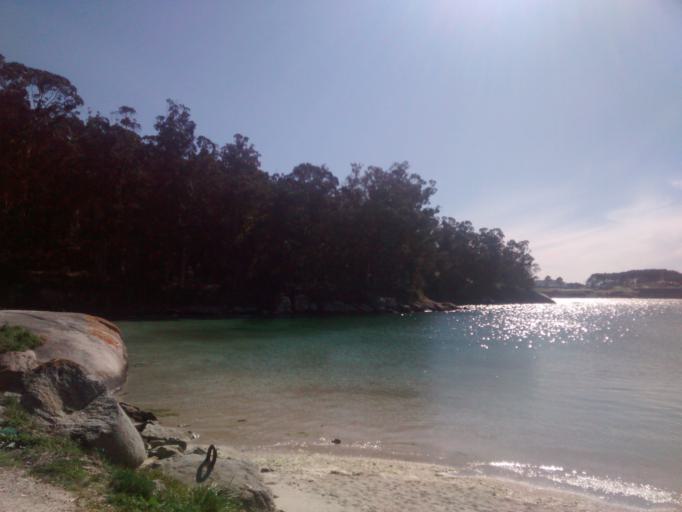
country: ES
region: Galicia
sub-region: Provincia de Pontevedra
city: O Grove
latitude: 42.4886
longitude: -8.8828
